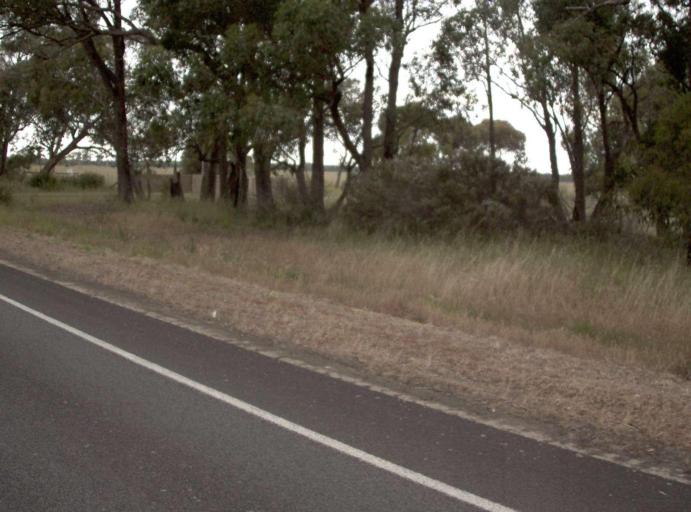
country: AU
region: Victoria
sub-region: Wellington
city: Sale
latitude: -38.4773
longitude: 146.9231
